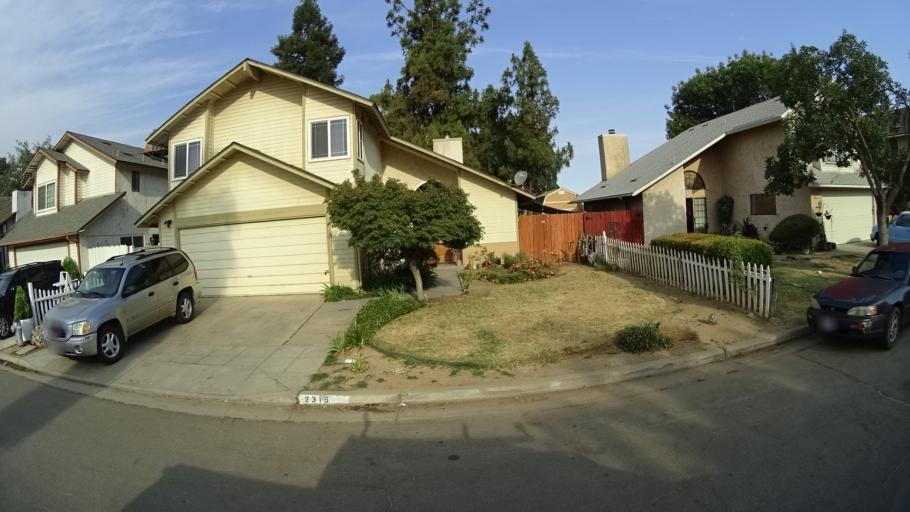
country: US
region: California
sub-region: Fresno County
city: West Park
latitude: 36.7703
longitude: -119.8508
